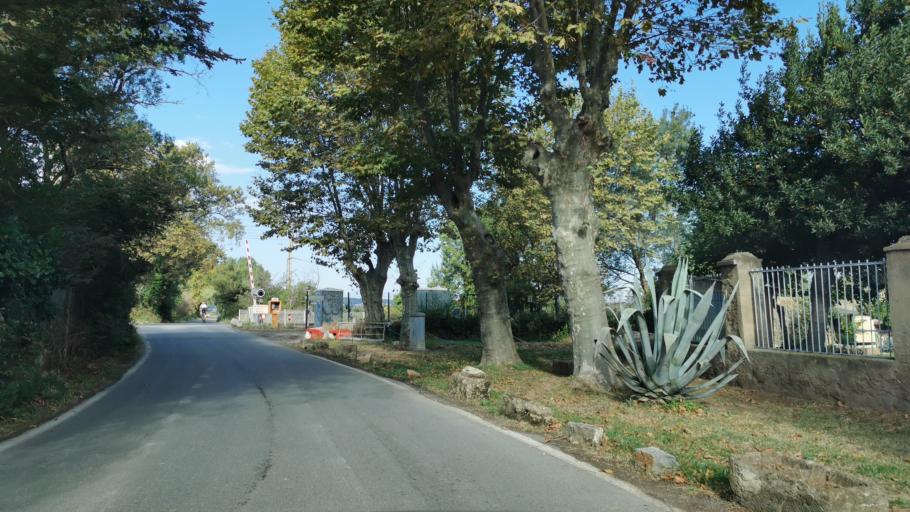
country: FR
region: Languedoc-Roussillon
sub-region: Departement de l'Aude
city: Gruissan
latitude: 43.1302
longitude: 3.0309
